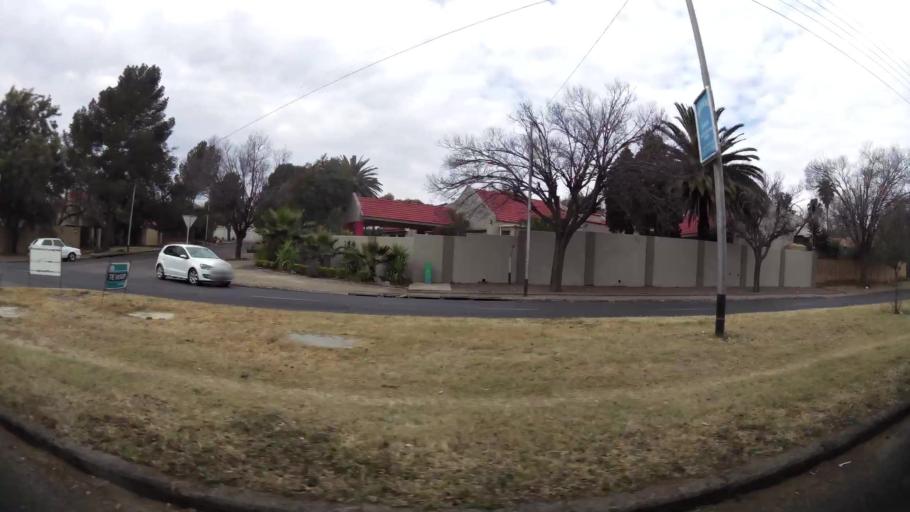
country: ZA
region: Orange Free State
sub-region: Mangaung Metropolitan Municipality
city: Bloemfontein
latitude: -29.0934
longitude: 26.2148
